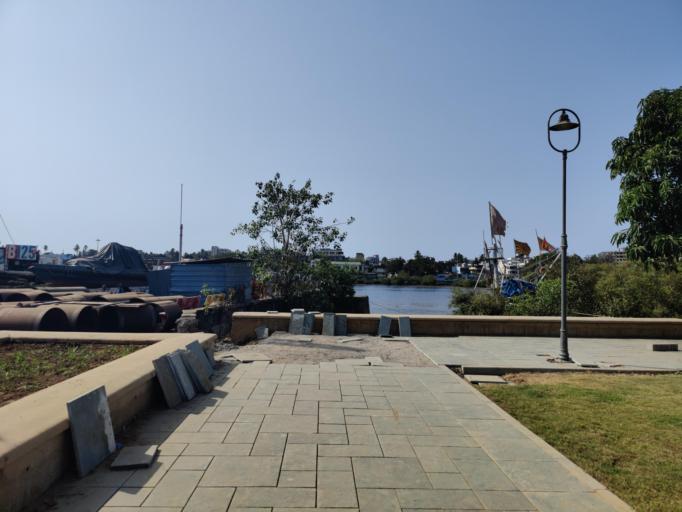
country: IN
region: Daman and Diu
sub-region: Daman District
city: Daman
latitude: 20.4102
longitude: 72.8346
